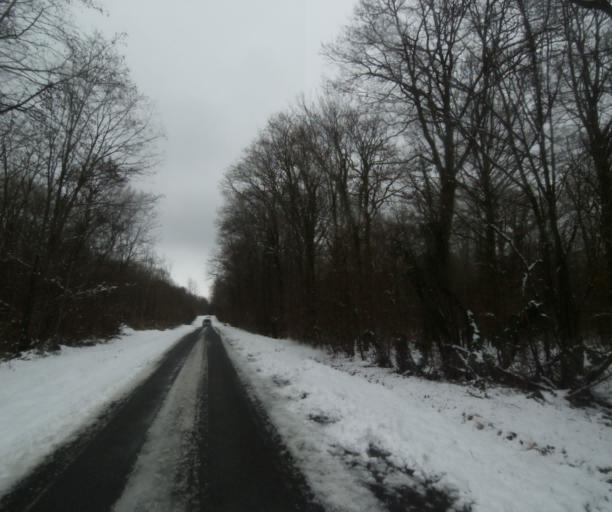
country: FR
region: Champagne-Ardenne
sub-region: Departement de la Haute-Marne
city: Laneuville-a-Remy
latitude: 48.5110
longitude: 4.8924
